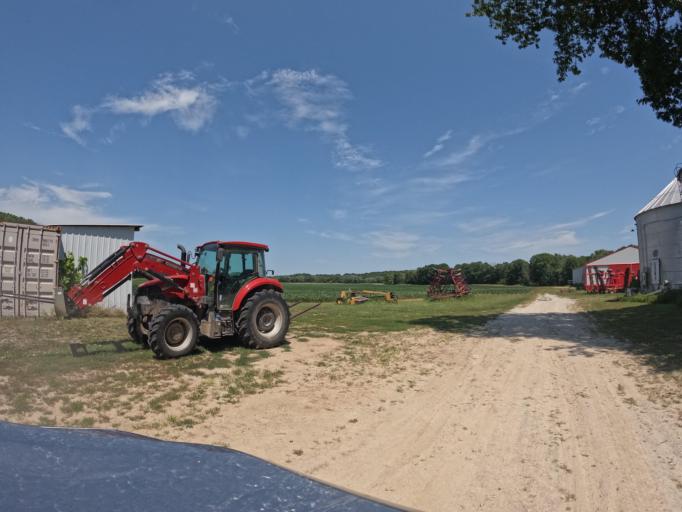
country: US
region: Iowa
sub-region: Henry County
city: Mount Pleasant
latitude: 40.8908
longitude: -91.6808
